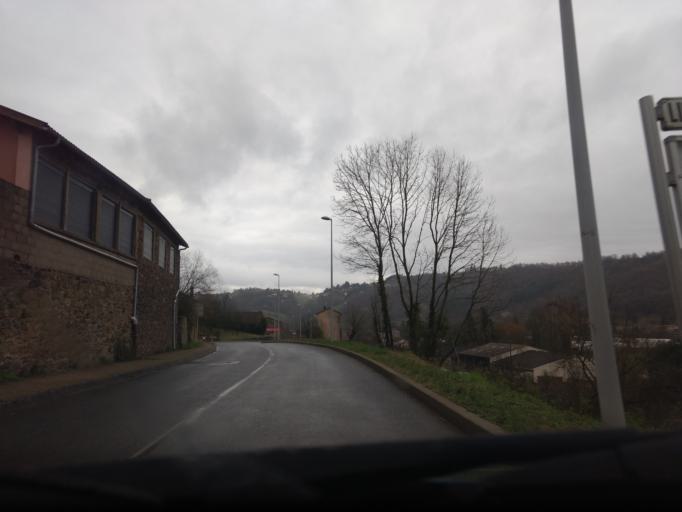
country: FR
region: Midi-Pyrenees
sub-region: Departement de l'Aveyron
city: Livinhac-le-Haut
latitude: 44.5917
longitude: 2.2287
